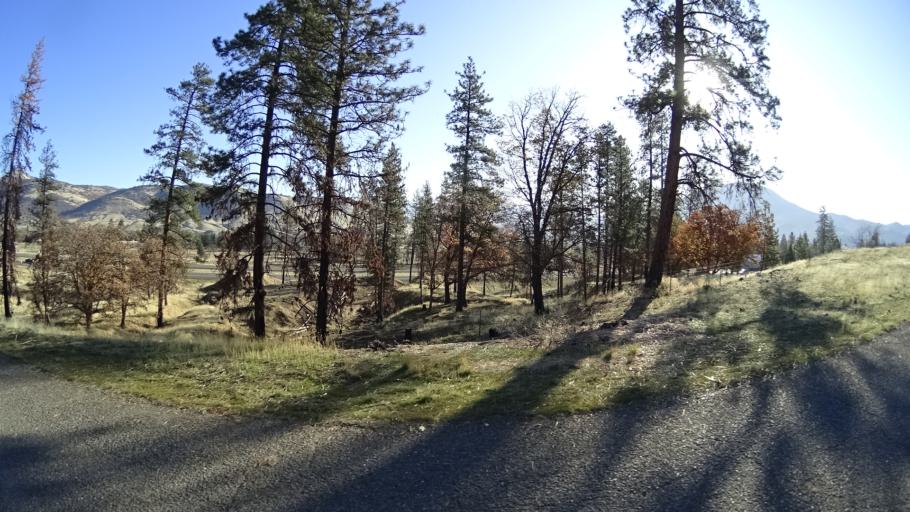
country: US
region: California
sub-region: Siskiyou County
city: Yreka
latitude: 41.9049
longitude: -122.5700
